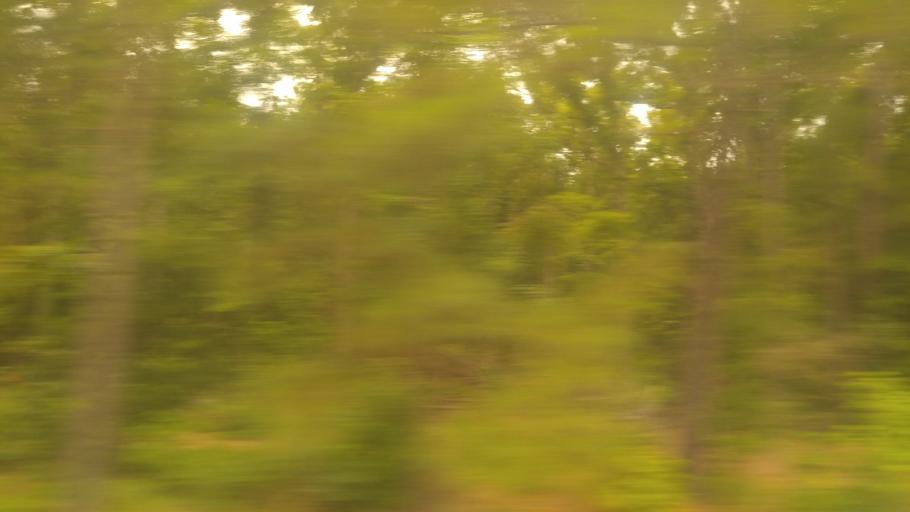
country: US
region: Virginia
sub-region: Henrico County
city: Glen Allen
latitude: 37.6793
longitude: -77.5030
